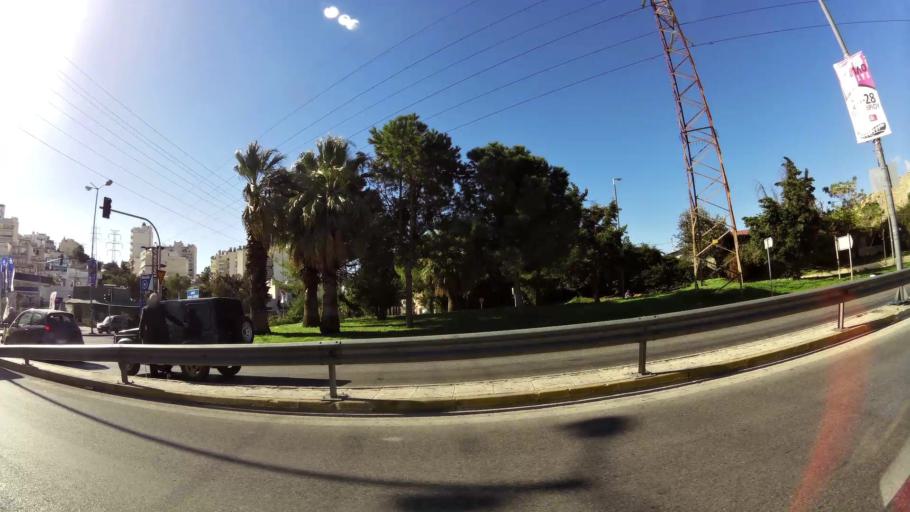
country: GR
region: Attica
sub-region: Nomos Piraios
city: Keratsini
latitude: 37.9646
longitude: 23.6129
